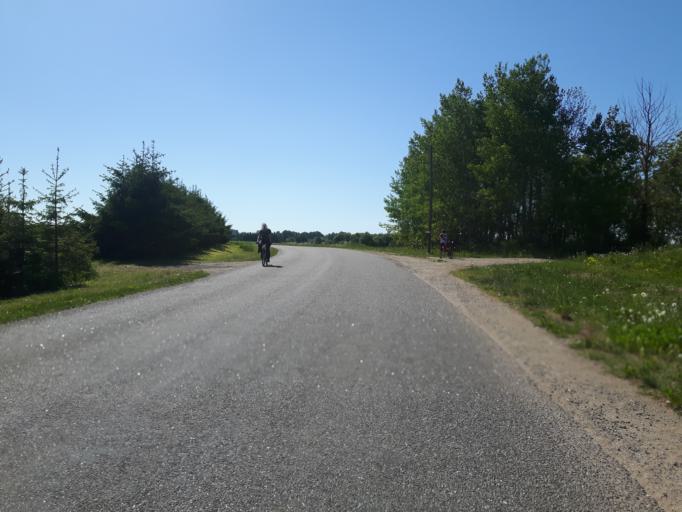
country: EE
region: Laeaene-Virumaa
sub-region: Haljala vald
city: Haljala
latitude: 59.5450
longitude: 26.1709
